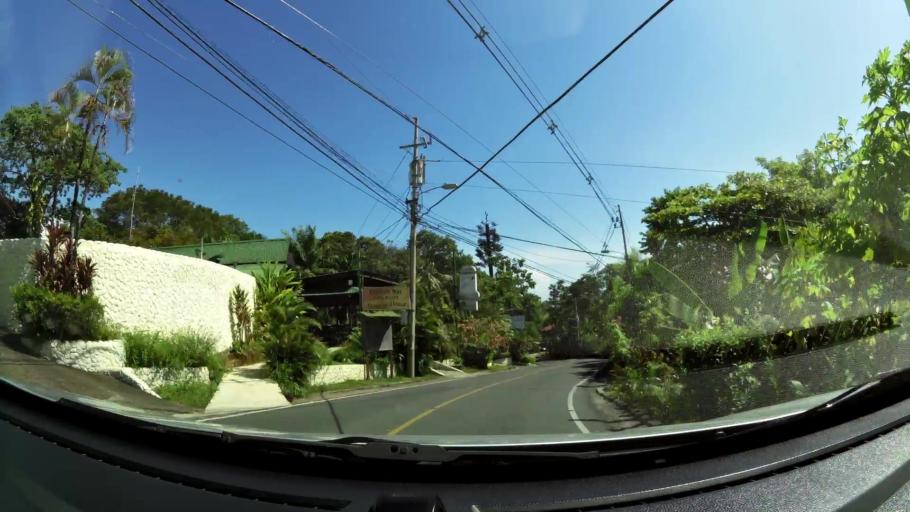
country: CR
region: Puntarenas
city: Quepos
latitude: 9.4054
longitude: -84.1565
